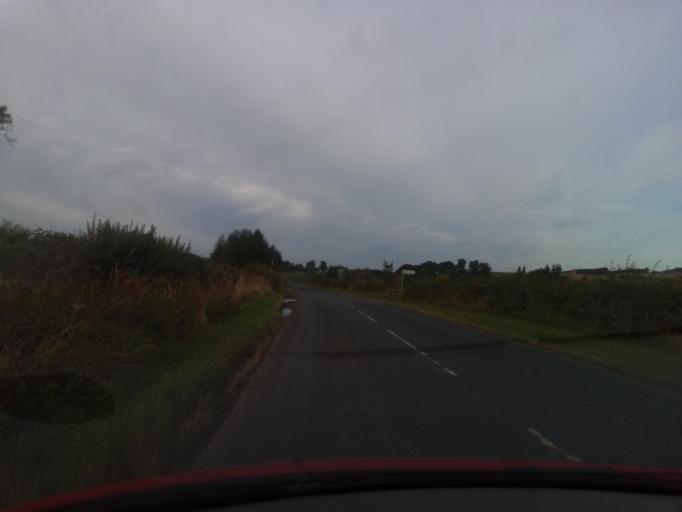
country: GB
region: Scotland
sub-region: The Scottish Borders
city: Kelso
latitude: 55.5223
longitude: -2.4004
